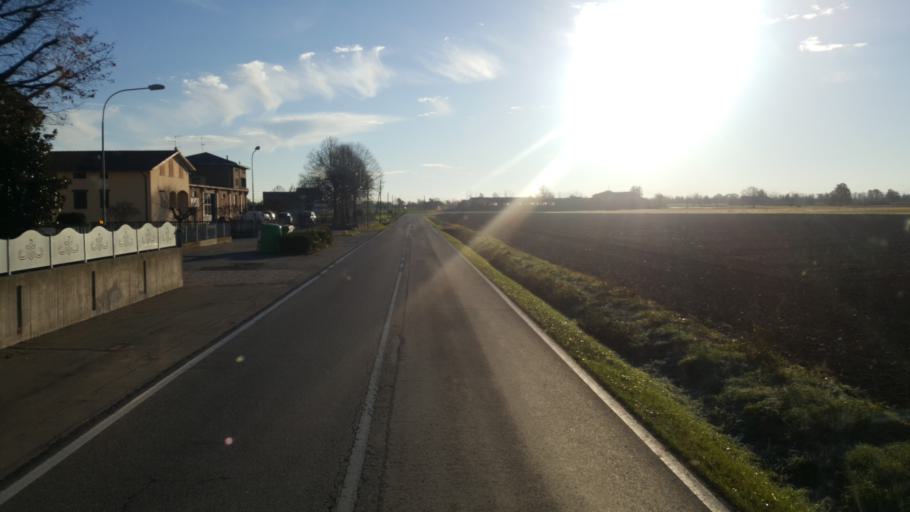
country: IT
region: Emilia-Romagna
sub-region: Provincia di Parma
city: Fontevivo
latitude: 44.8517
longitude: 10.1931
